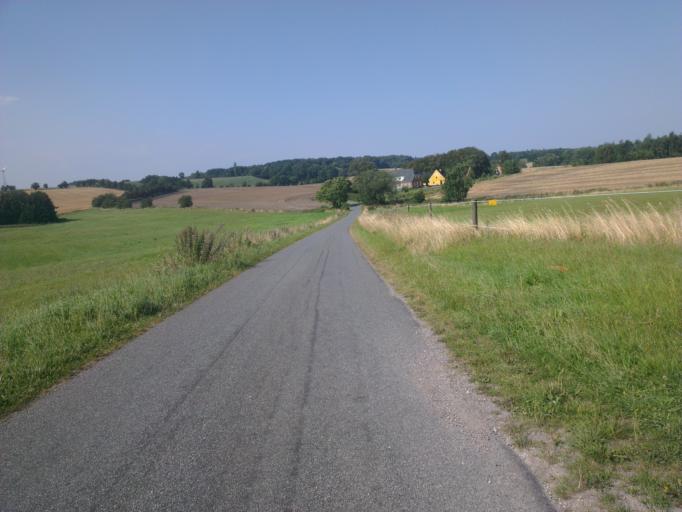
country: DK
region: Capital Region
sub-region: Frederikssund Kommune
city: Skibby
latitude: 55.7544
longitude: 11.9464
